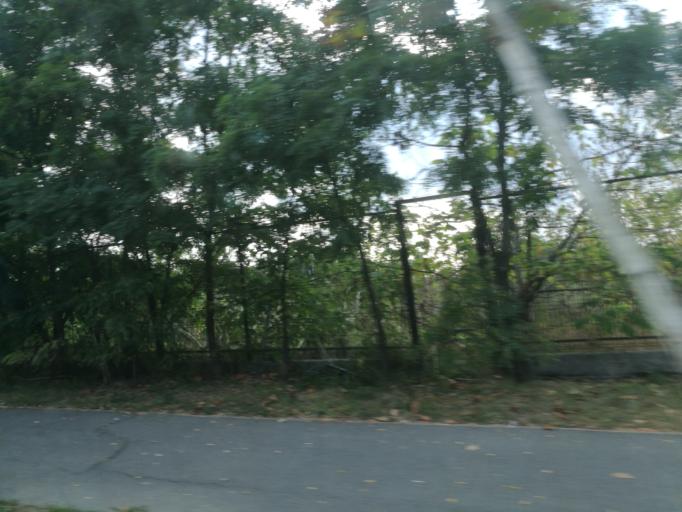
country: RO
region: Ilfov
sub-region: Comuna Mogosoaia
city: Mogosoaia
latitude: 44.5058
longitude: 26.0255
